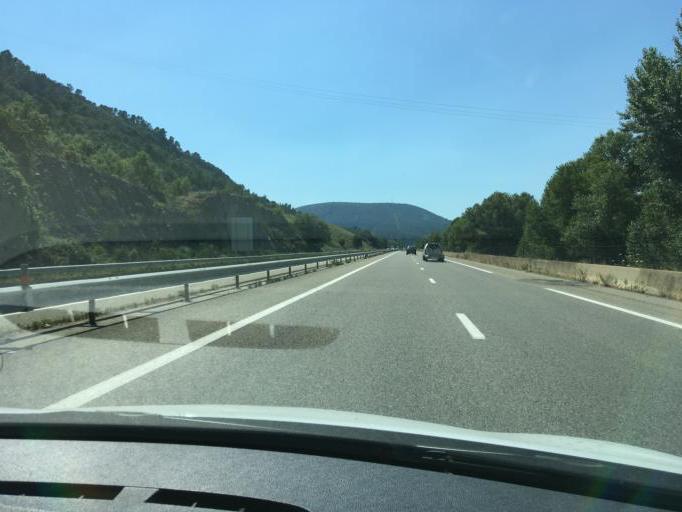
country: FR
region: Provence-Alpes-Cote d'Azur
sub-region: Departement du Vaucluse
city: Beaumont-de-Pertuis
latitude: 43.6896
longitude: 5.6995
